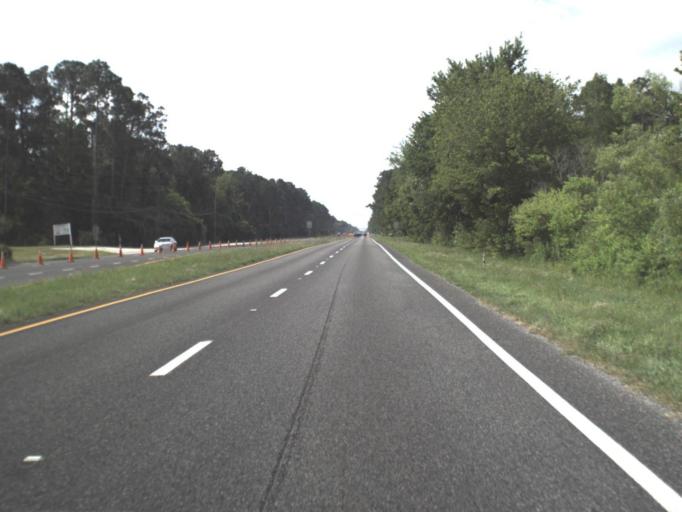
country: US
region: Florida
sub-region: Saint Johns County
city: Saint Augustine Shores
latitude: 29.7998
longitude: -81.3204
